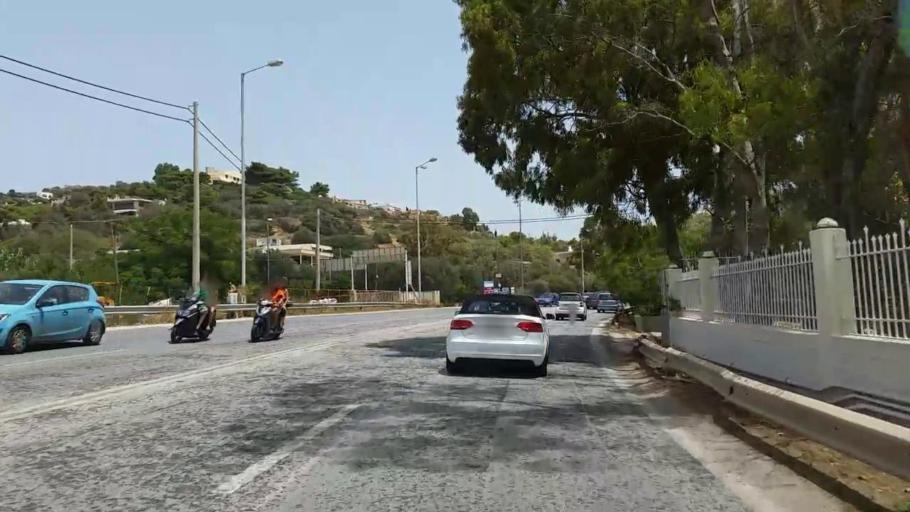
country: GR
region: Attica
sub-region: Nomarchia Anatolikis Attikis
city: Agios Dimitrios Kropias
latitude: 37.8022
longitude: 23.8681
